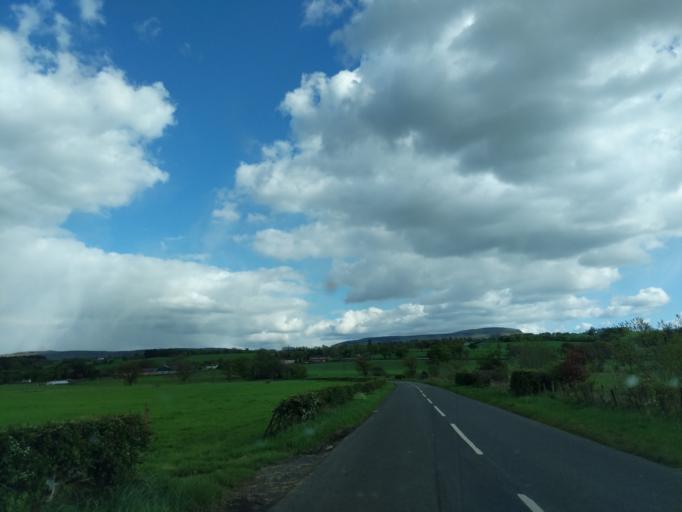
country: GB
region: Scotland
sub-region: Stirling
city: Balfron
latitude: 56.1315
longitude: -4.2439
